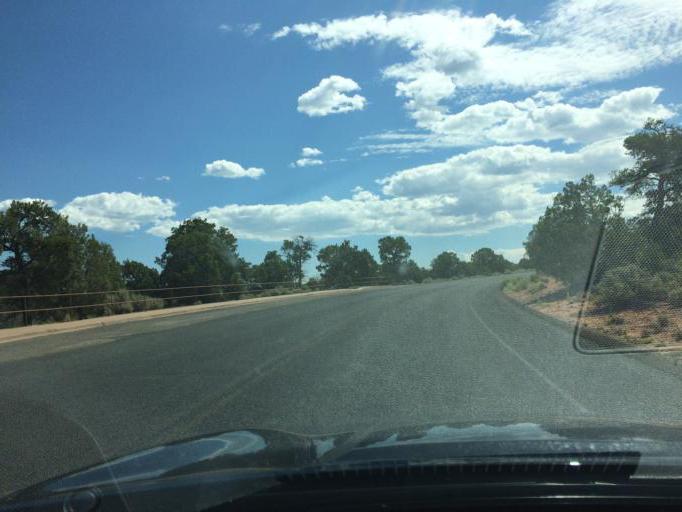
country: US
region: Arizona
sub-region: Apache County
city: Chinle
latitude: 36.1042
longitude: -109.3687
